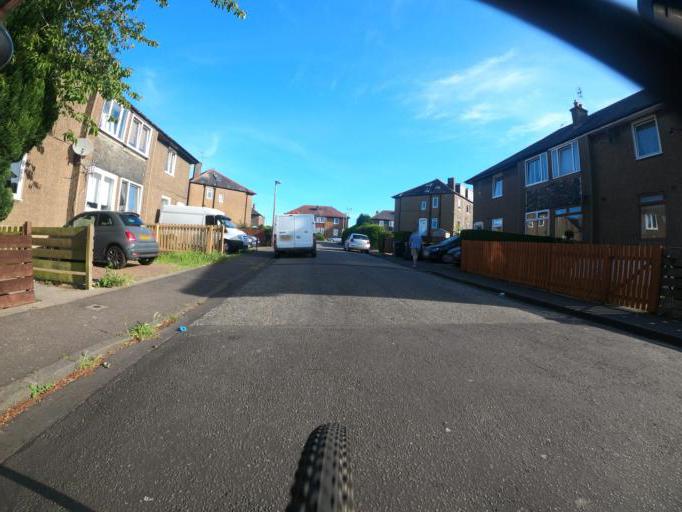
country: GB
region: Scotland
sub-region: Edinburgh
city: Edinburgh
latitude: 55.9731
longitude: -3.2339
